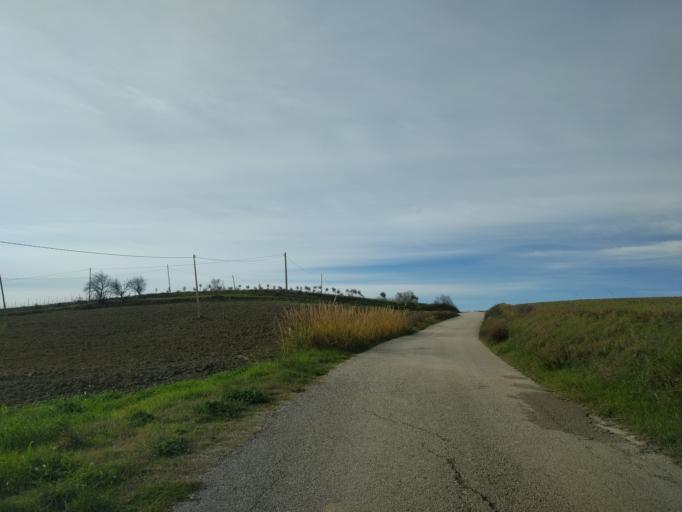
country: IT
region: The Marches
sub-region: Provincia di Pesaro e Urbino
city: Cuccurano
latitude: 43.8104
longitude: 12.9307
